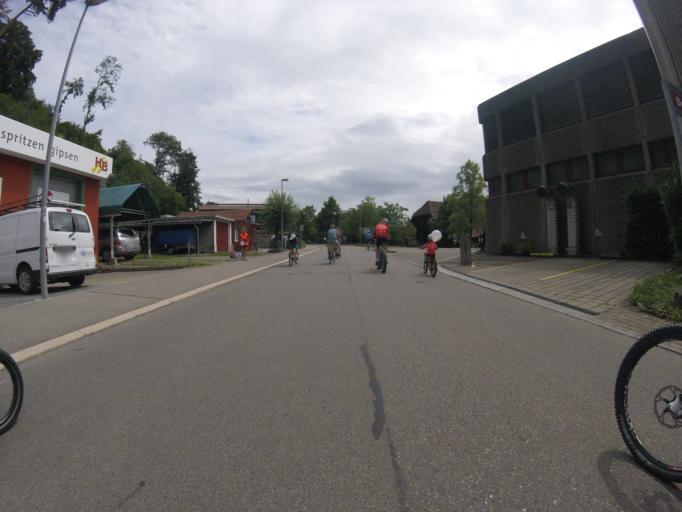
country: CH
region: Bern
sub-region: Bern-Mittelland District
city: Muri
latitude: 46.9362
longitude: 7.5034
